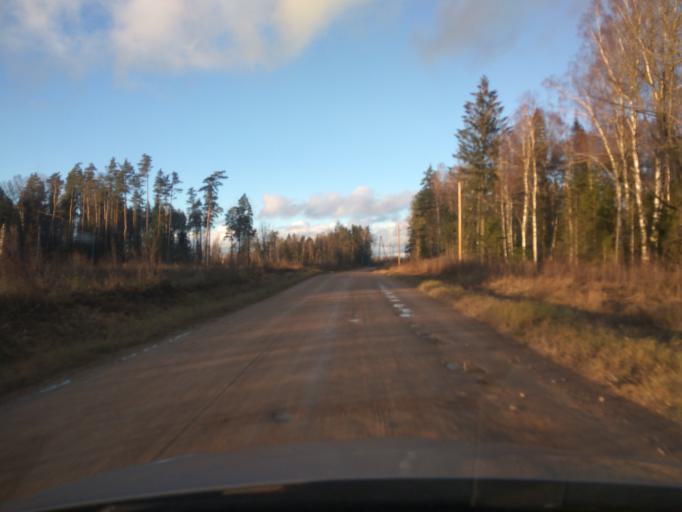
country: LV
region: Aizpute
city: Aizpute
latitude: 56.7861
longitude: 21.7922
